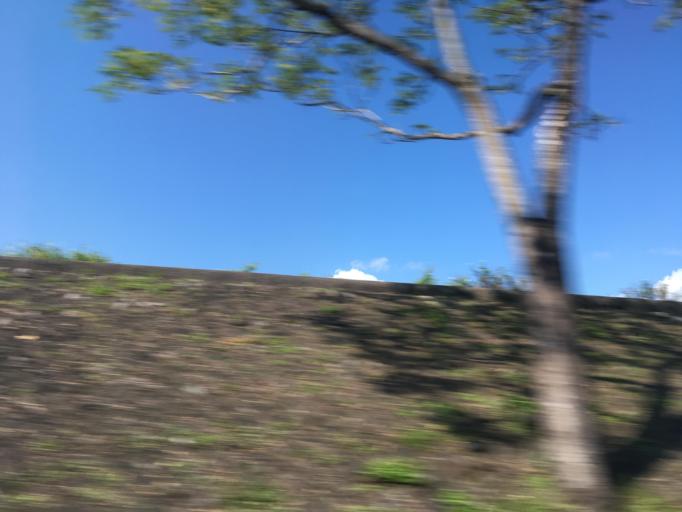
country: TW
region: Taiwan
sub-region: Yilan
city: Yilan
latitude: 24.7566
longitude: 121.7323
